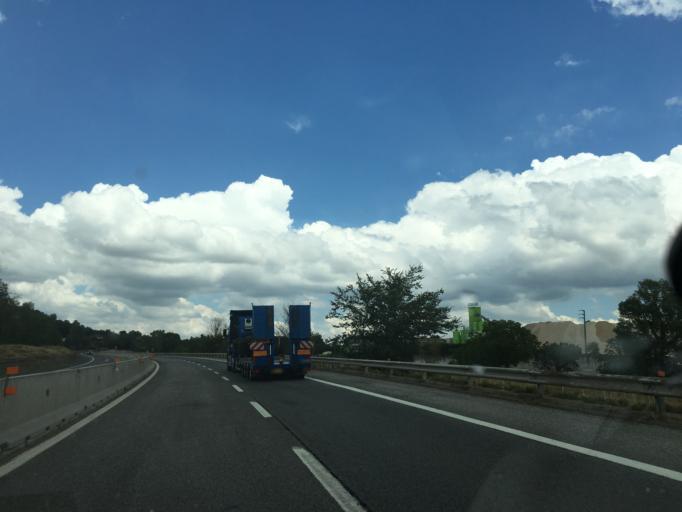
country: IT
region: Campania
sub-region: Provincia di Avellino
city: Passo di Mirabella-Pianopantano
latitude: 41.0588
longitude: 15.0342
